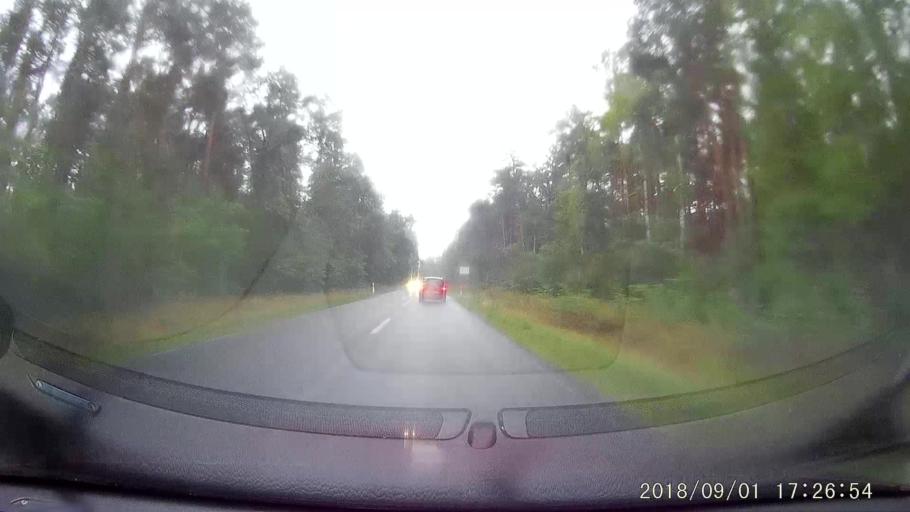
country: PL
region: Lubusz
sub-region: Powiat zaganski
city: Zagan
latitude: 51.6723
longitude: 15.3090
